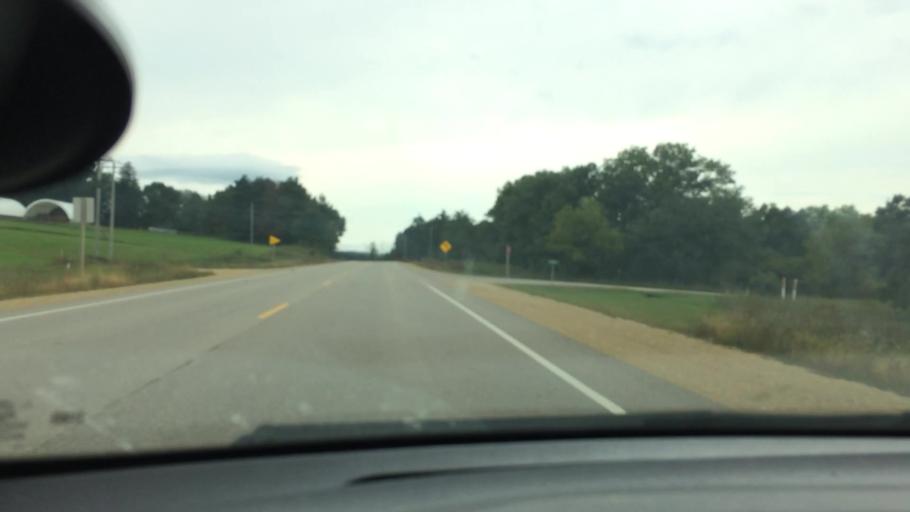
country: US
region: Wisconsin
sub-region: Trempealeau County
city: Osseo
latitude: 44.5897
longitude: -91.1685
